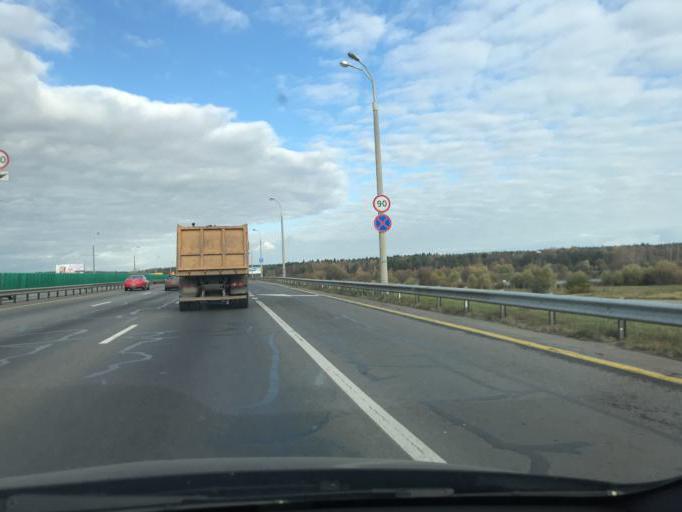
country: BY
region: Minsk
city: Zhdanovichy
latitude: 53.9559
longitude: 27.4526
